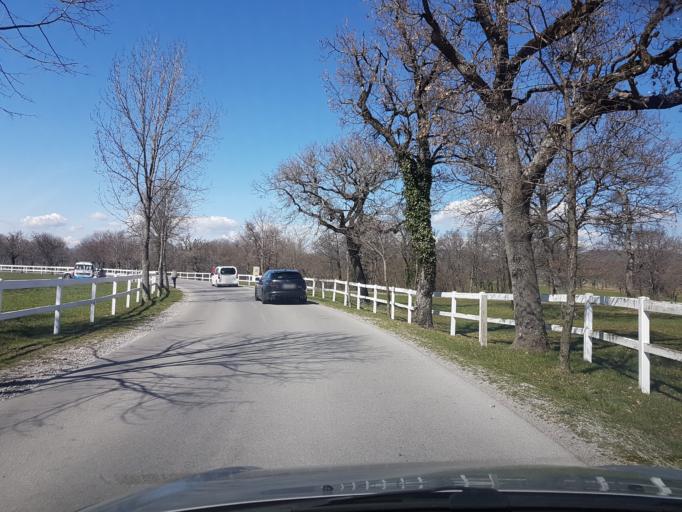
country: SI
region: Sezana
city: Sezana
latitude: 45.6694
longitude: 13.8879
